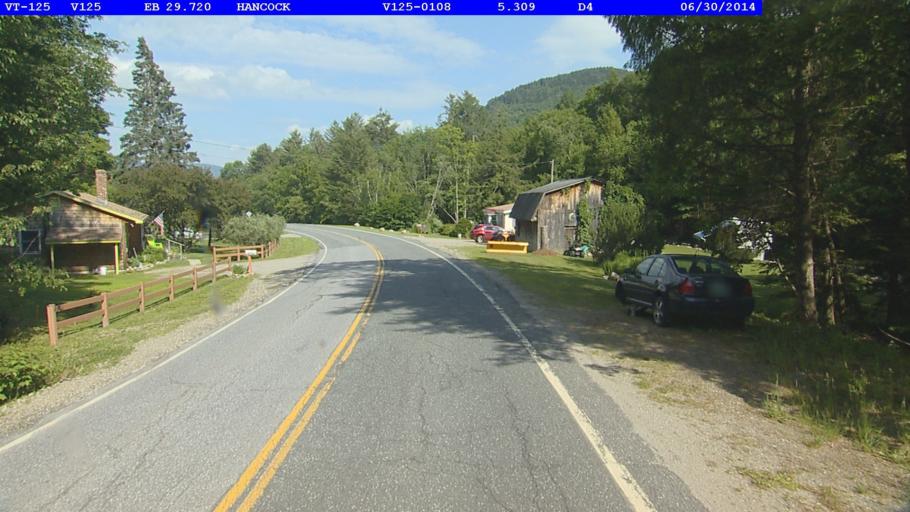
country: US
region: Vermont
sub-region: Orange County
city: Randolph
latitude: 43.9268
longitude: -72.8773
